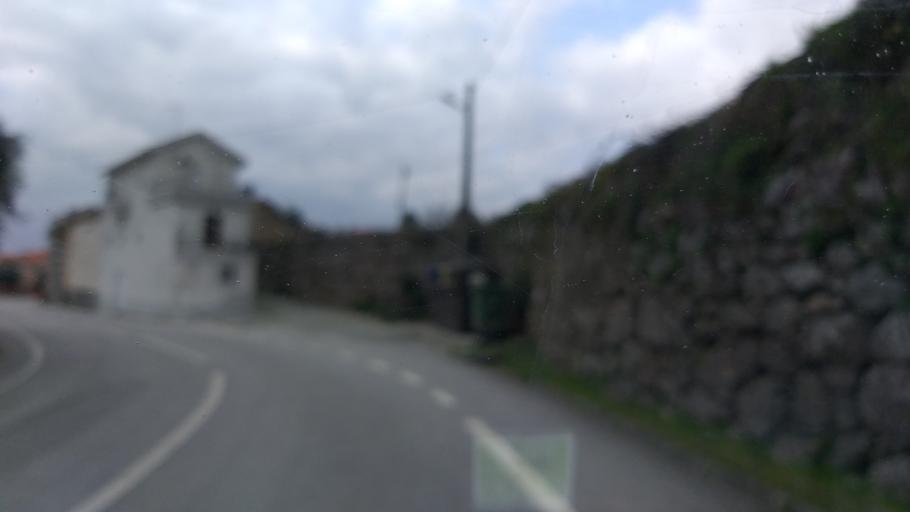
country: PT
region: Guarda
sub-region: Seia
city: Seia
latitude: 40.4761
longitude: -7.6320
